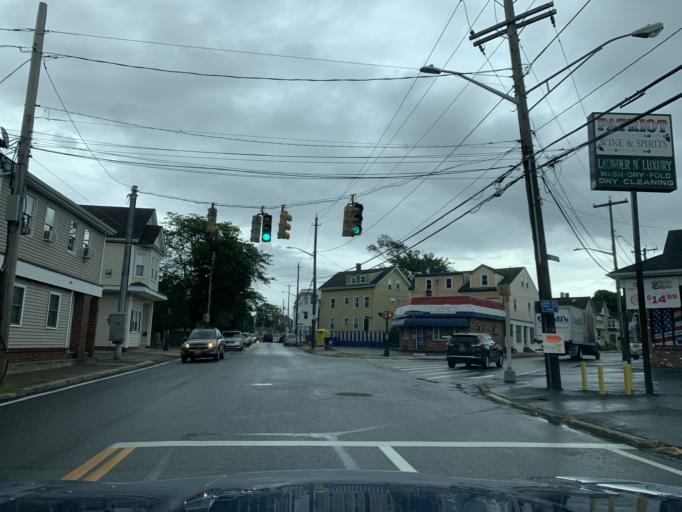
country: US
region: Rhode Island
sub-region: Bristol County
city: Warren
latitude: 41.7358
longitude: -71.2857
